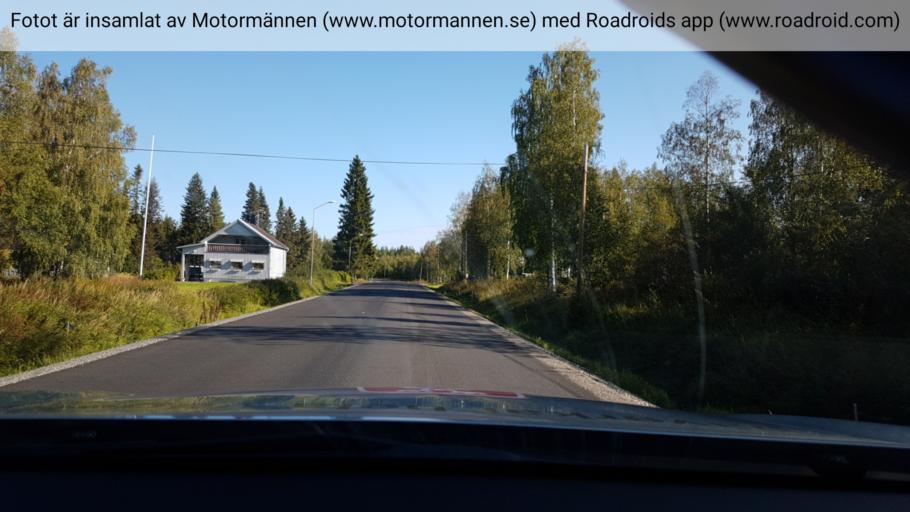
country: SE
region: Vaesterbotten
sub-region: Norsjo Kommun
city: Norsjoe
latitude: 64.8970
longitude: 19.4648
